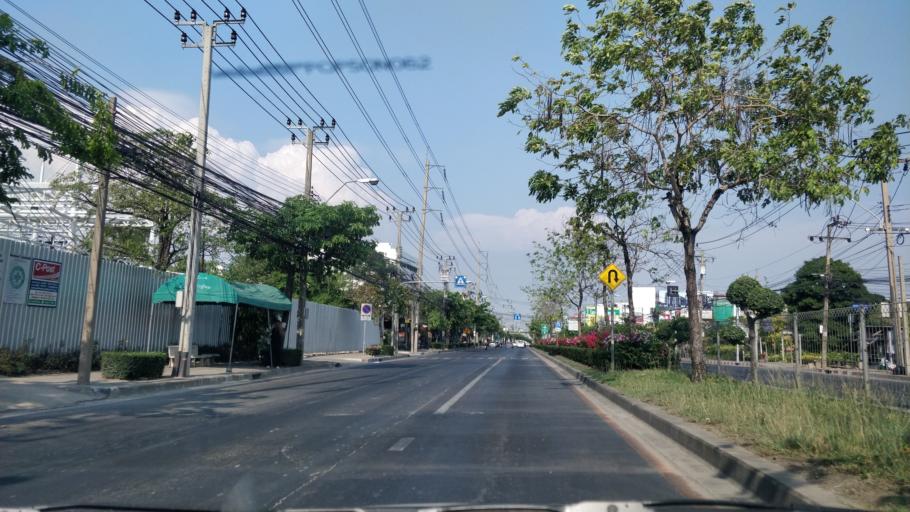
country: TH
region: Bangkok
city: Suan Luang
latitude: 13.7181
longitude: 100.6641
